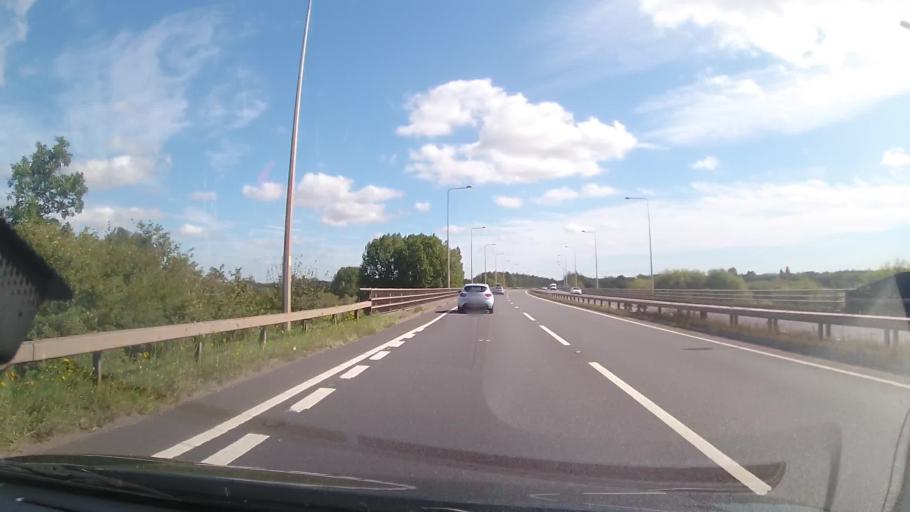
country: GB
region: England
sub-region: Staffordshire
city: Tamworth
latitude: 52.6249
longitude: -1.6987
